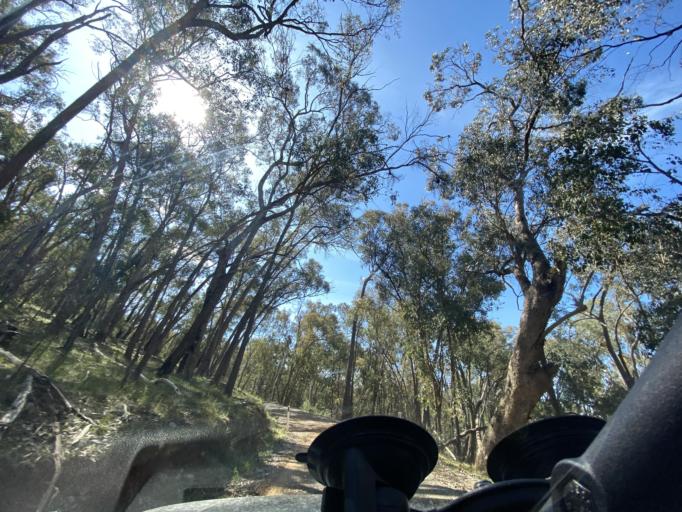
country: AU
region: Victoria
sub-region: Mansfield
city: Mansfield
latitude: -36.8009
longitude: 146.1164
